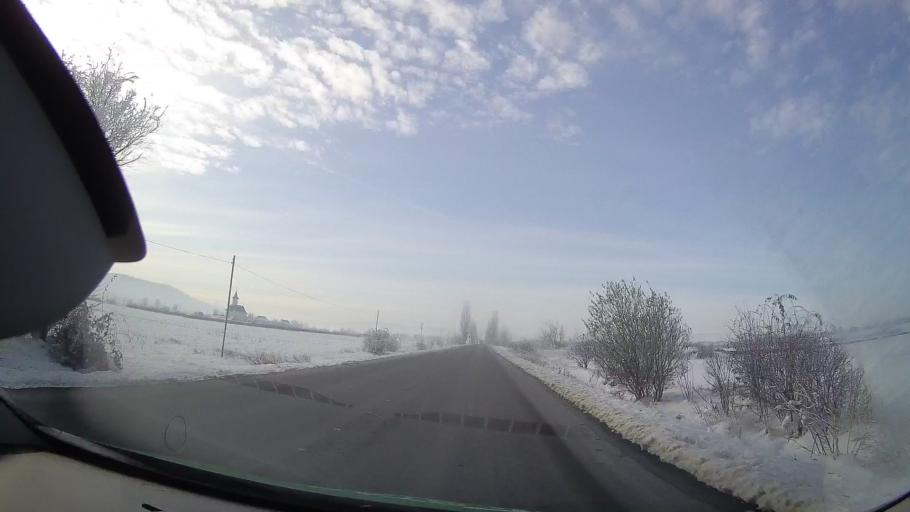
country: RO
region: Neamt
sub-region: Comuna Timisesti
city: Dumbrava
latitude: 47.2150
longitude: 26.4390
